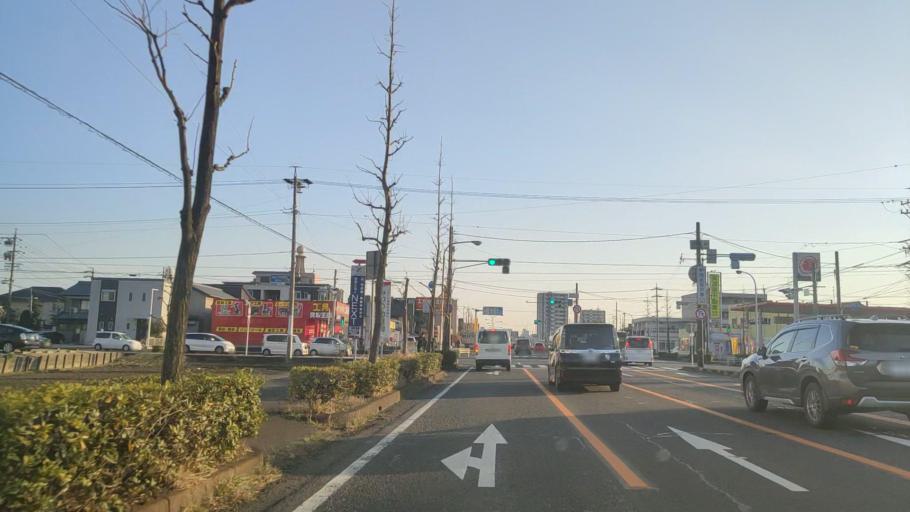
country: JP
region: Gifu
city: Gifu-shi
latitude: 35.4091
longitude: 136.7272
